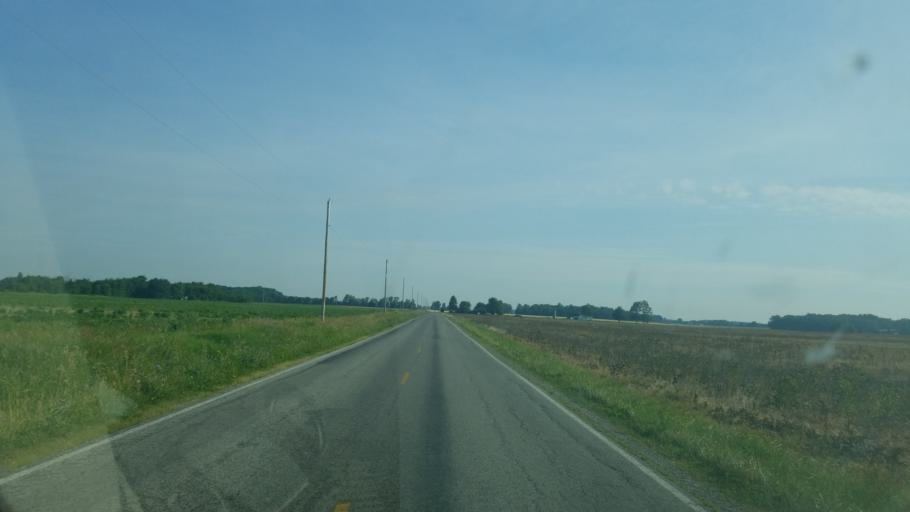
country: US
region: Ohio
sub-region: Hancock County
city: Arlington
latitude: 40.9002
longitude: -83.6985
